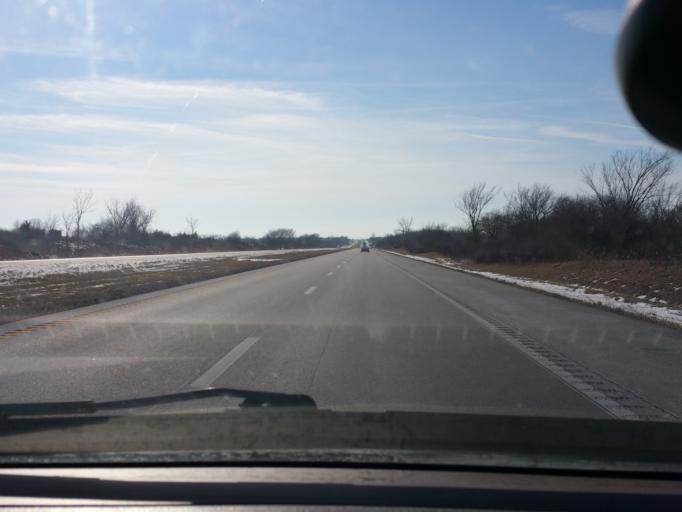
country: US
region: Missouri
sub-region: Clinton County
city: Cameron
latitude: 39.8303
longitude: -94.1872
